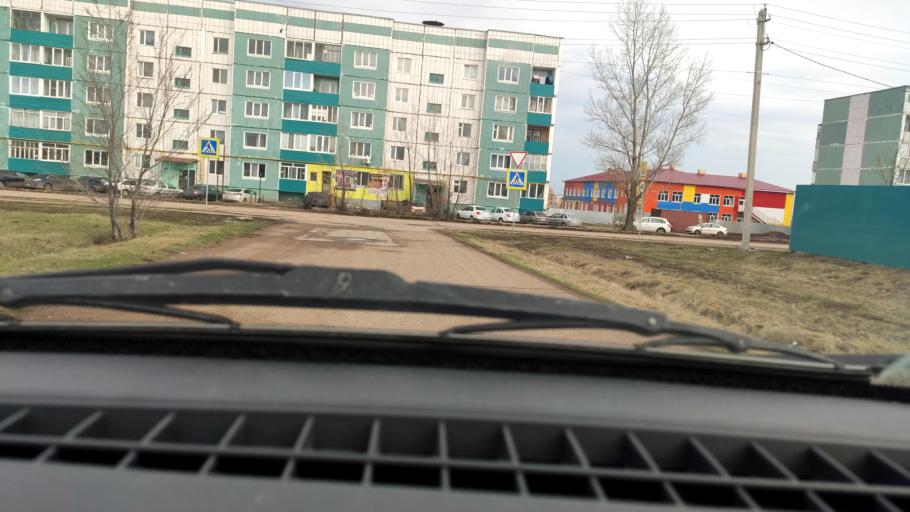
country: RU
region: Bashkortostan
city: Davlekanovo
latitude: 54.2286
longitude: 55.0320
